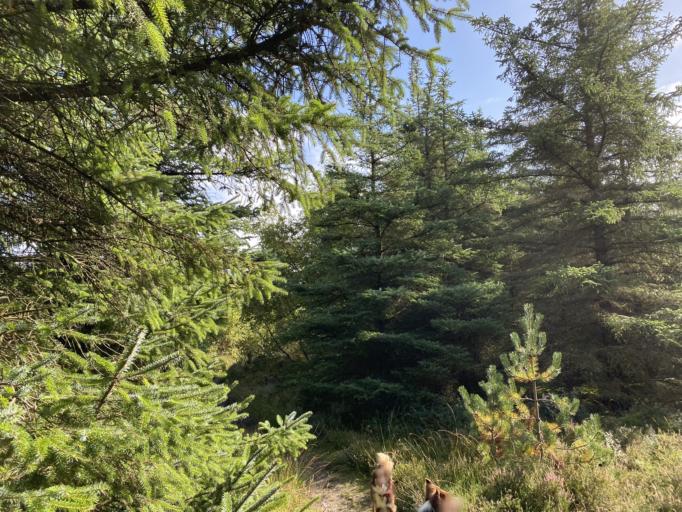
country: DK
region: Central Jutland
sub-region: Holstebro Kommune
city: Ulfborg
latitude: 56.3159
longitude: 8.1362
